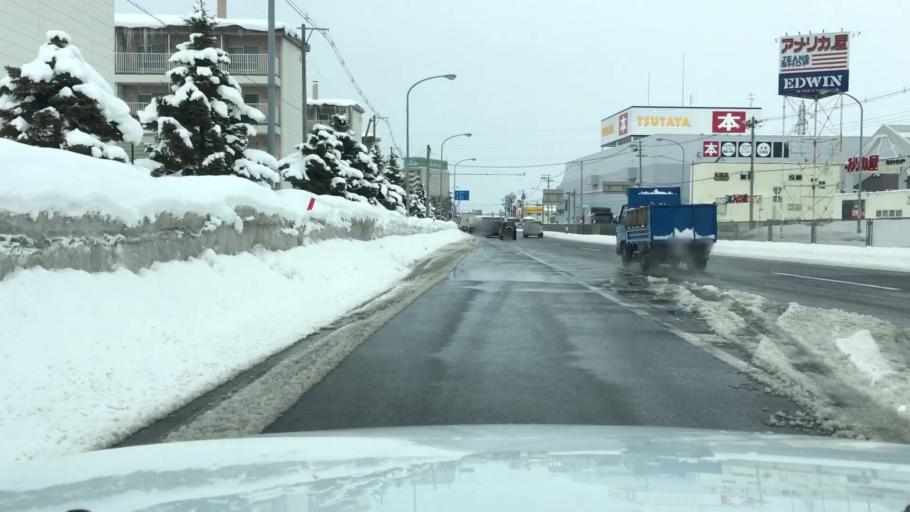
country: JP
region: Aomori
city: Hirosaki
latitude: 40.5992
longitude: 140.5015
